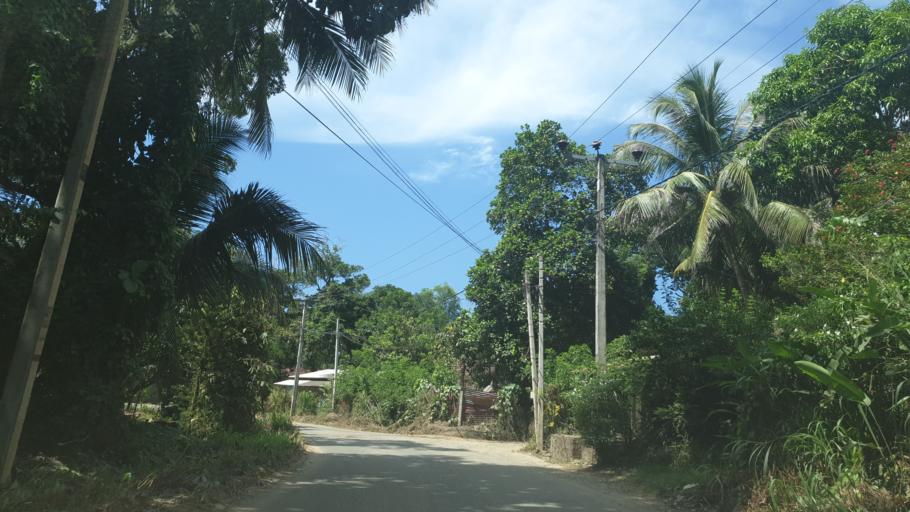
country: LK
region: Southern
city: Matara
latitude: 5.9761
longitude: 80.6610
